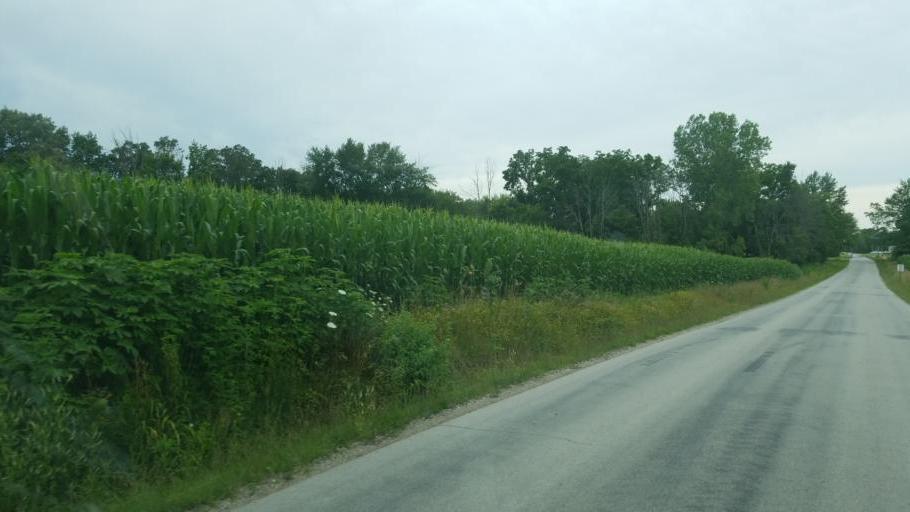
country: US
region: Ohio
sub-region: Knox County
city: Centerburg
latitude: 40.2861
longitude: -82.6989
